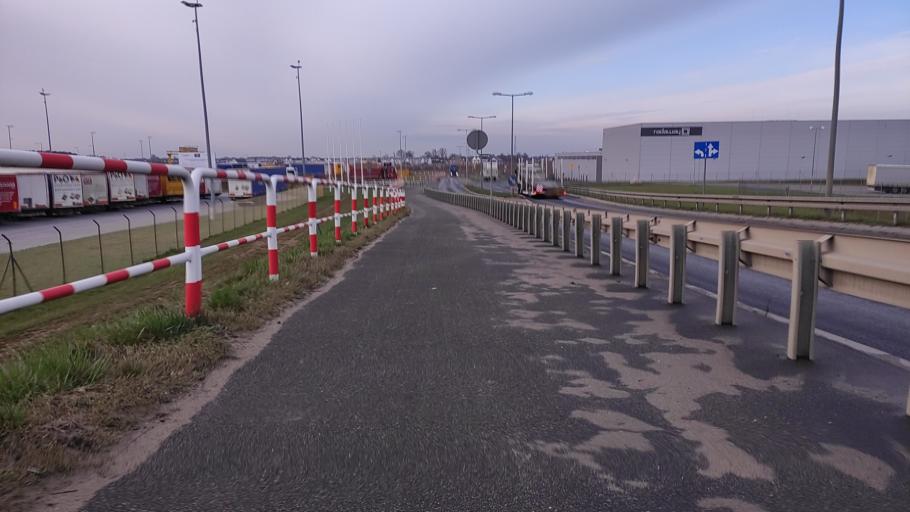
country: PL
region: Greater Poland Voivodeship
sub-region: Powiat poznanski
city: Swarzedz
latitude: 52.3996
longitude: 17.1219
